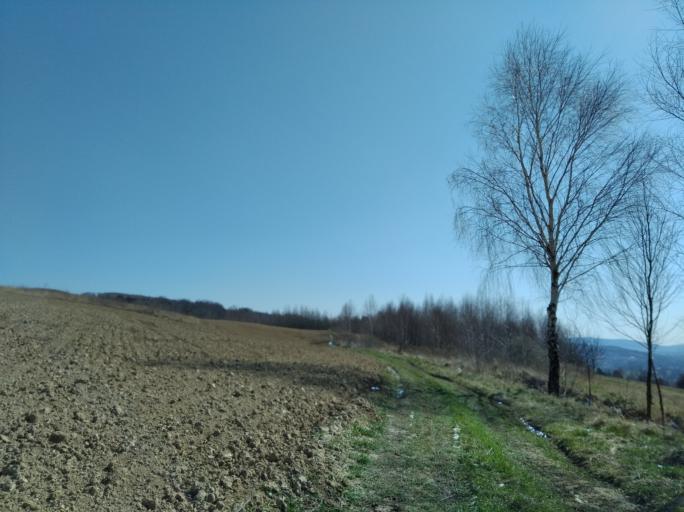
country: PL
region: Subcarpathian Voivodeship
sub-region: Powiat strzyzowski
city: Strzyzow
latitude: 49.8539
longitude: 21.8113
